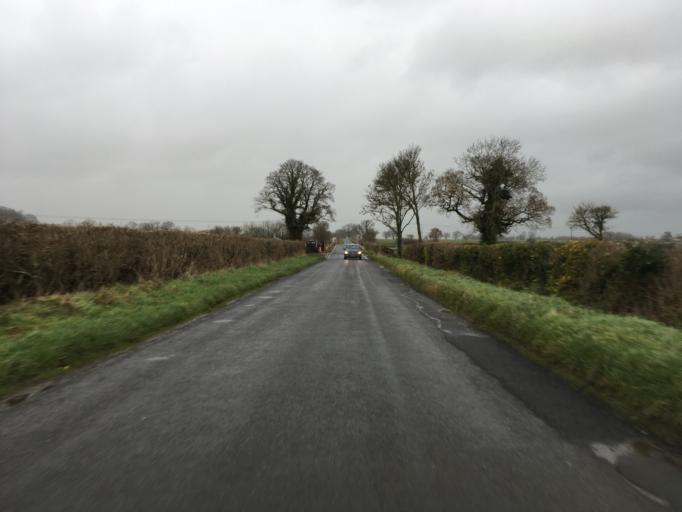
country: GB
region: England
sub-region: Wiltshire
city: Norton
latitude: 51.5433
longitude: -2.2012
